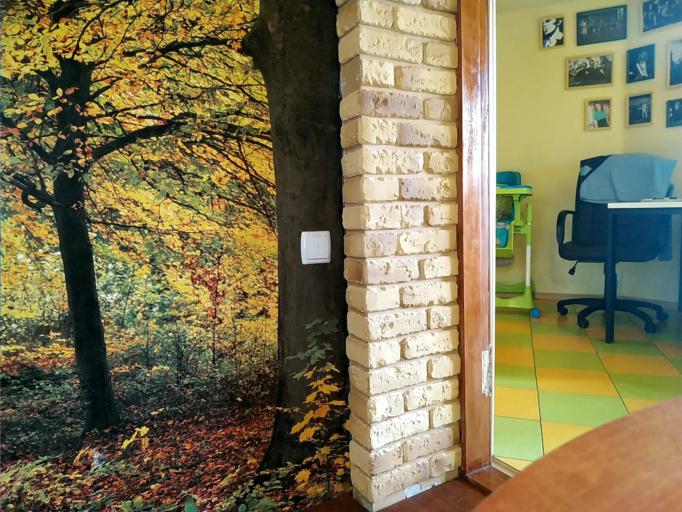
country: RU
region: Jaroslavl
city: Krasnyy Profintern
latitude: 58.0459
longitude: 40.4486
